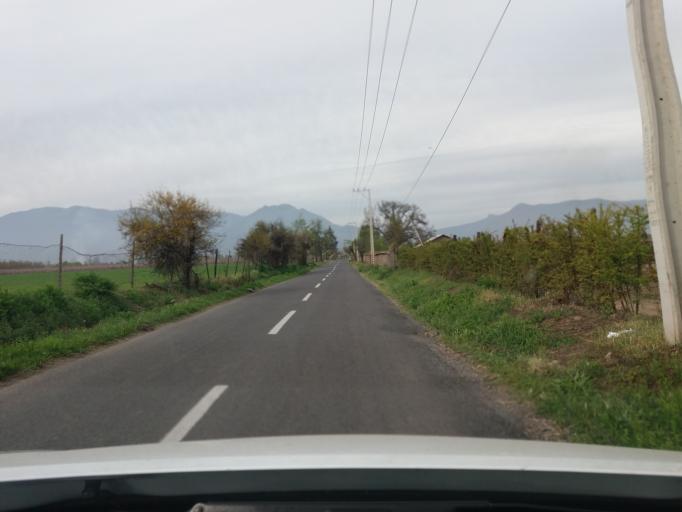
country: CL
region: Valparaiso
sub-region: Provincia de Los Andes
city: Los Andes
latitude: -32.8300
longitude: -70.6599
